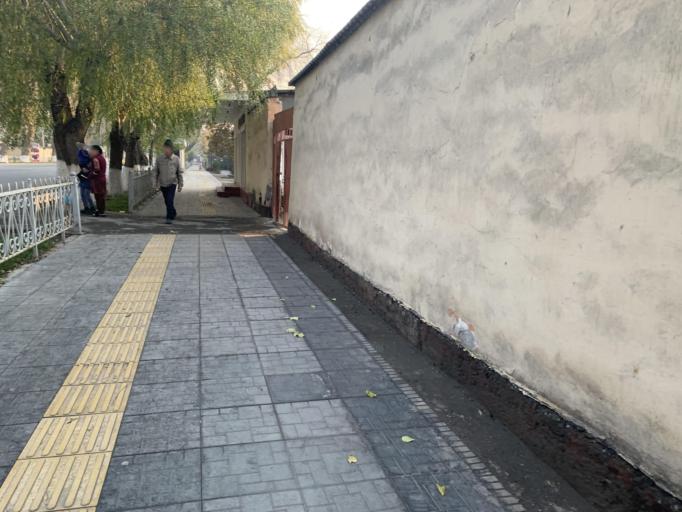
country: UZ
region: Fergana
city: Qo`qon
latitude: 40.5333
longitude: 70.9377
